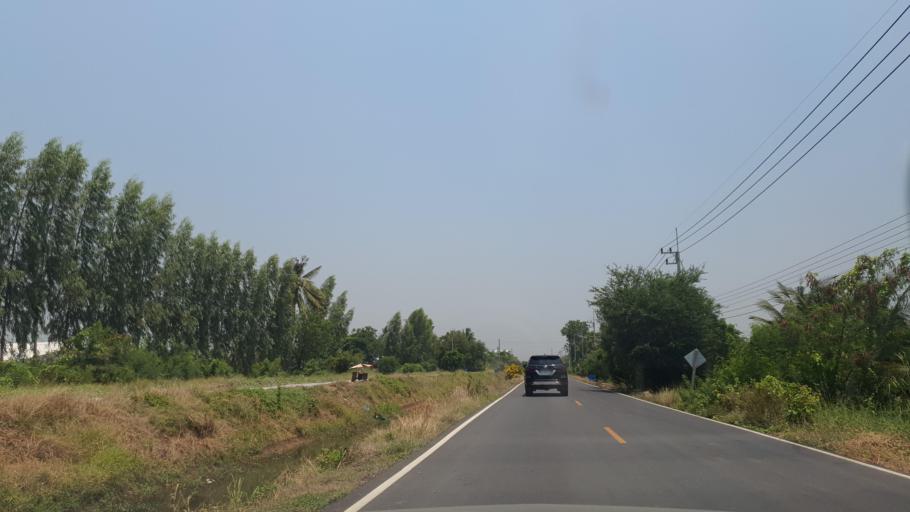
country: TH
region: Suphan Buri
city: Si Prachan
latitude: 14.6026
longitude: 100.1013
